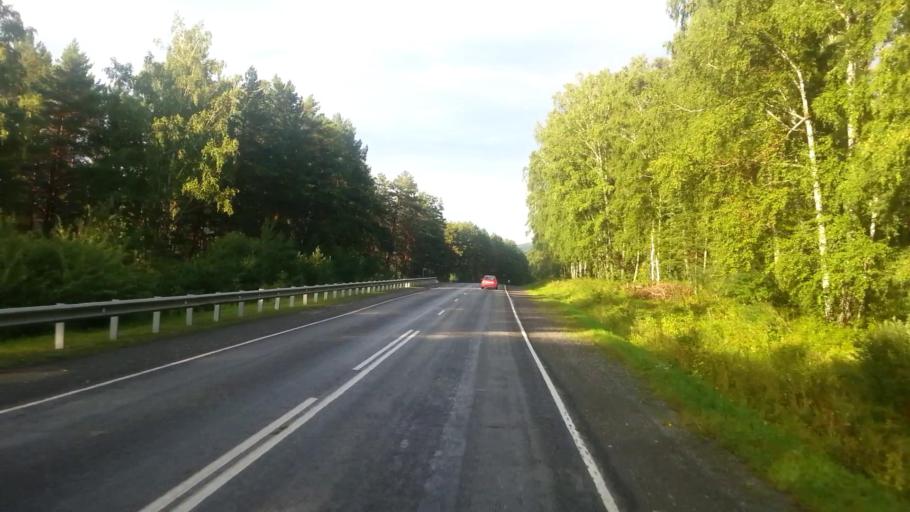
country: RU
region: Altay
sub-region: Mayminskiy Rayon
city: Manzherok
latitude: 51.8116
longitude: 85.7624
